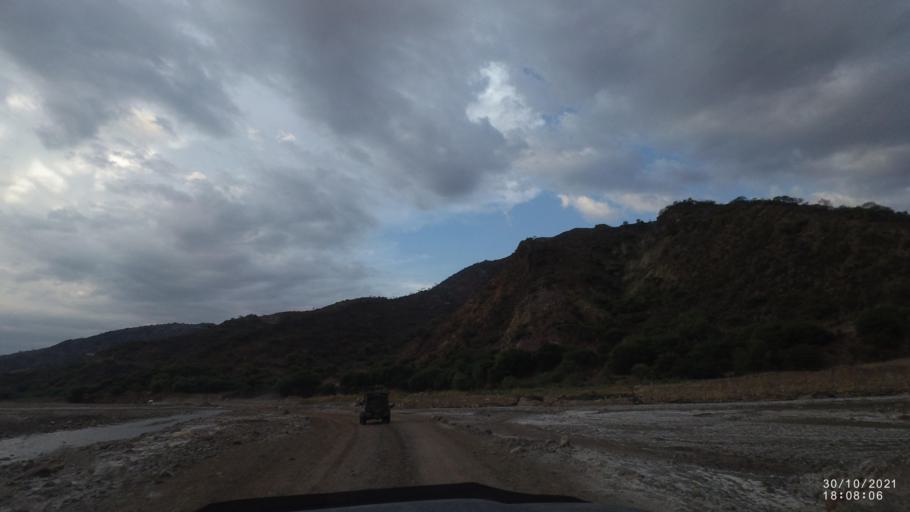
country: BO
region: Cochabamba
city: Sipe Sipe
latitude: -17.5609
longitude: -66.4490
